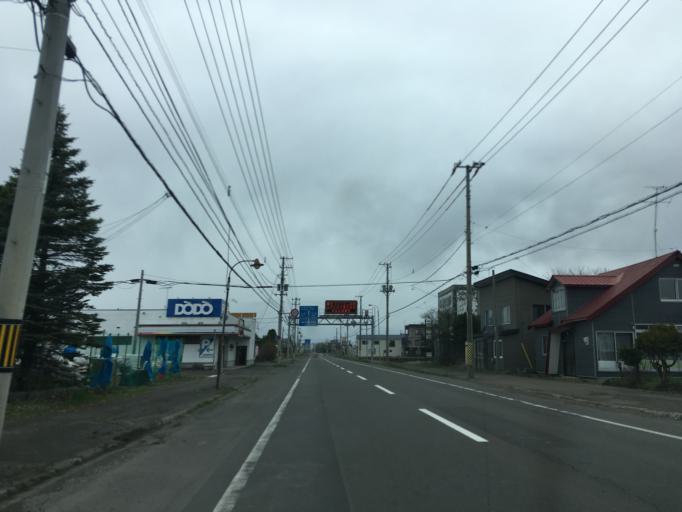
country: JP
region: Hokkaido
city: Chitose
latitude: 42.9466
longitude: 141.8033
